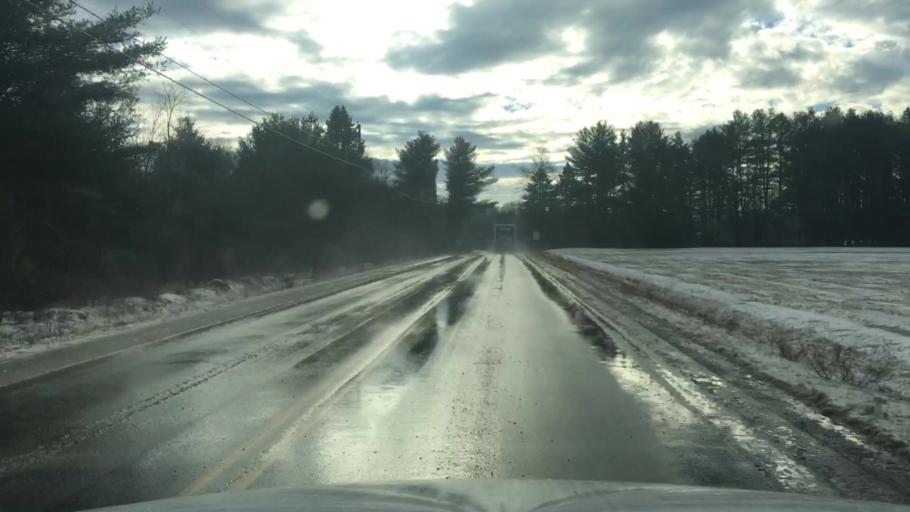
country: US
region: Maine
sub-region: Penobscot County
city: Brewer
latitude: 44.7441
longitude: -68.7659
